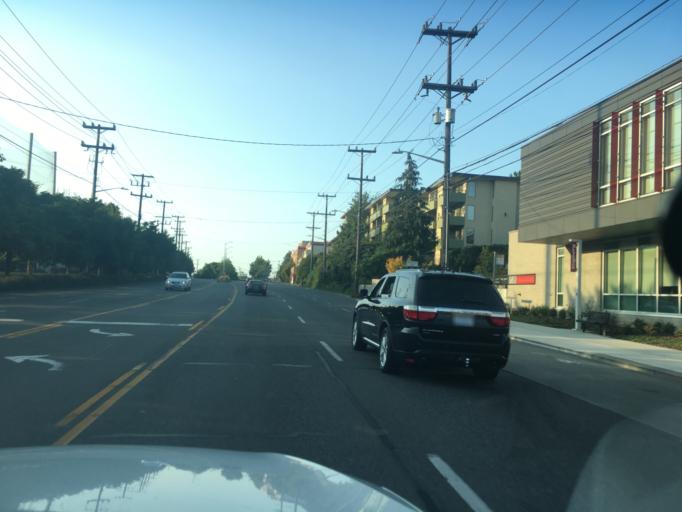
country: US
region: Washington
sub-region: King County
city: Seattle
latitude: 47.6452
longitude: -122.3759
